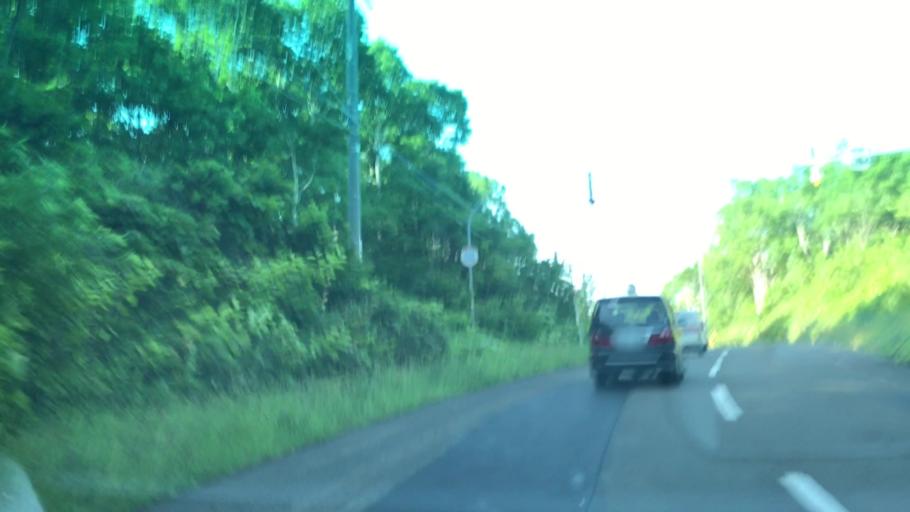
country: JP
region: Hokkaido
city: Otaru
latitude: 43.1300
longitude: 141.0122
